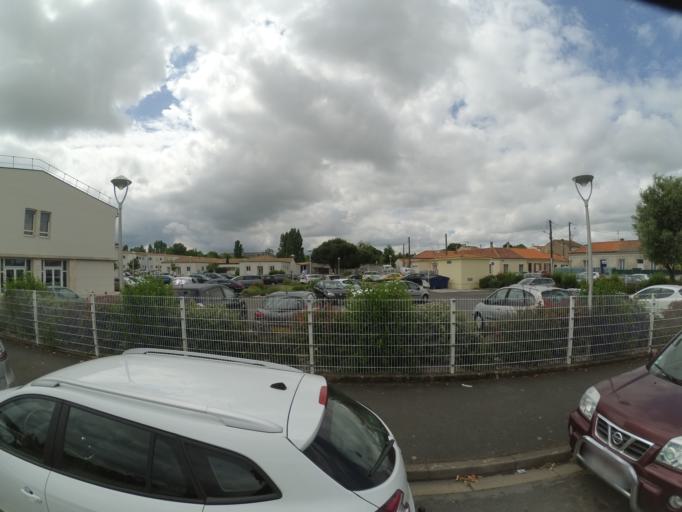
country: FR
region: Poitou-Charentes
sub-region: Departement de la Charente-Maritime
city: Rochefort
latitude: 45.9472
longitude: -0.9650
